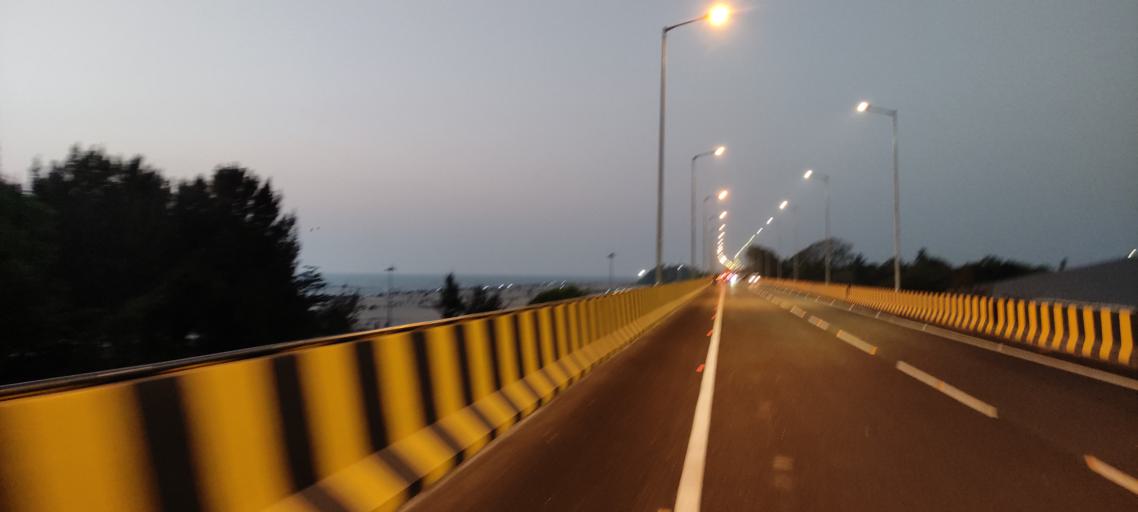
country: IN
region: Kerala
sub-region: Alappuzha
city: Alleppey
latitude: 9.4877
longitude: 76.3198
